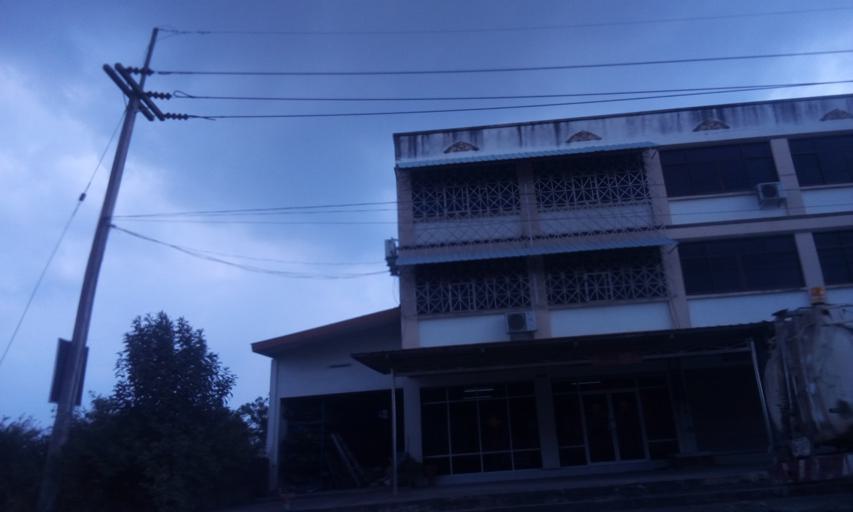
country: TH
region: Chon Buri
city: Ban Bueng
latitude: 13.2953
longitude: 101.1770
